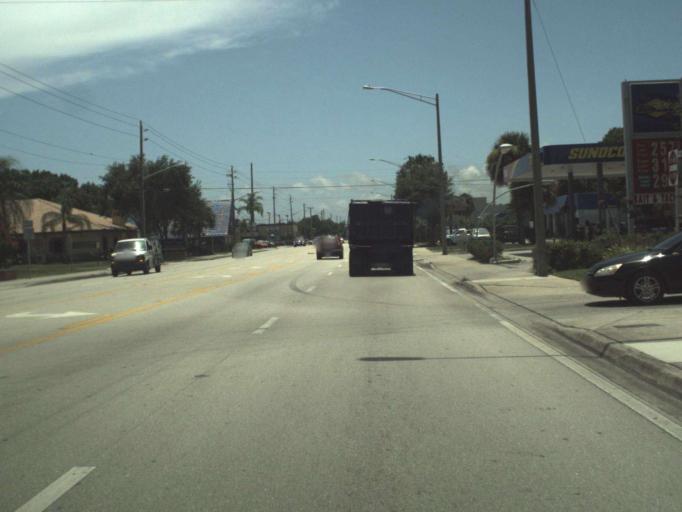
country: US
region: Florida
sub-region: Indian River County
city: Vero Beach
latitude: 27.6369
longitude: -80.3892
